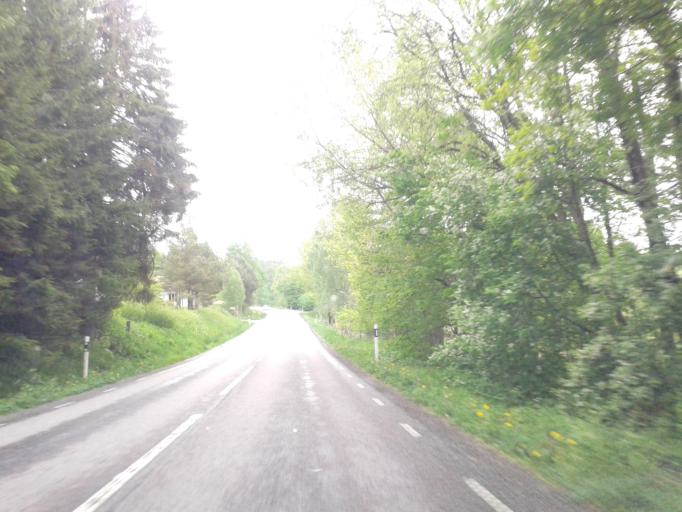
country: SE
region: Vaestra Goetaland
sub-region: Kungalvs Kommun
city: Kode
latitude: 57.8932
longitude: 11.8551
